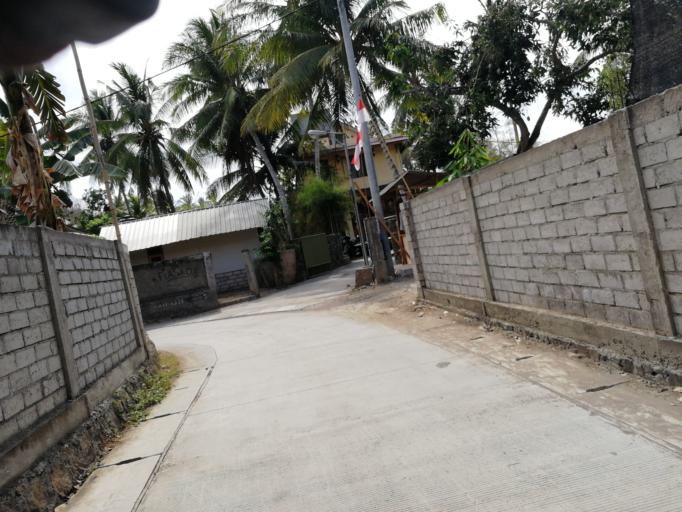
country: ID
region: West Nusa Tenggara
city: Kute
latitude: -8.8831
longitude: 116.2733
